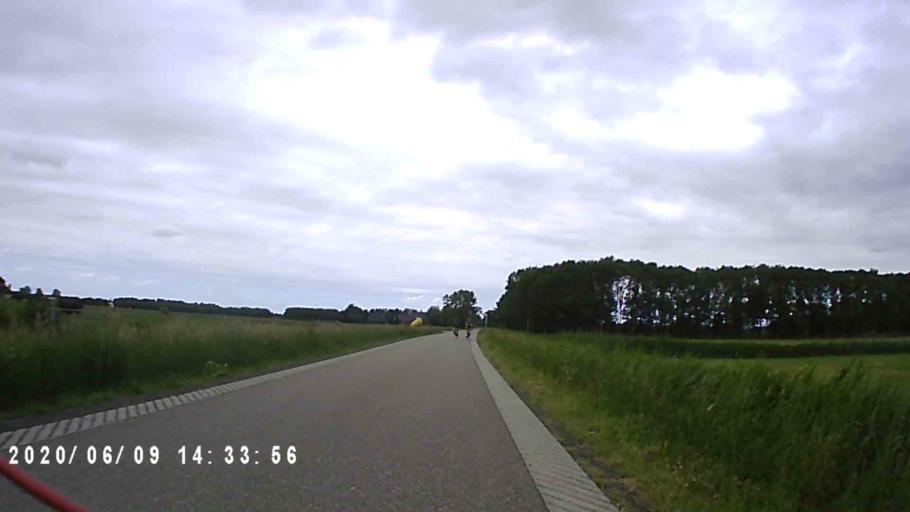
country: NL
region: Groningen
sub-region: Gemeente Bedum
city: Bedum
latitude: 53.3247
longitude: 6.5905
